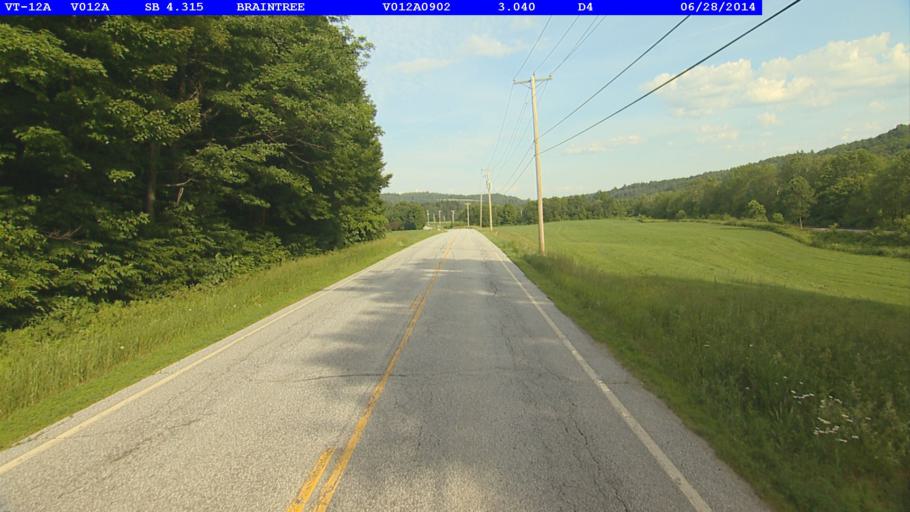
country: US
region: Vermont
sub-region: Orange County
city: Randolph
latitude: 43.9573
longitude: -72.7290
